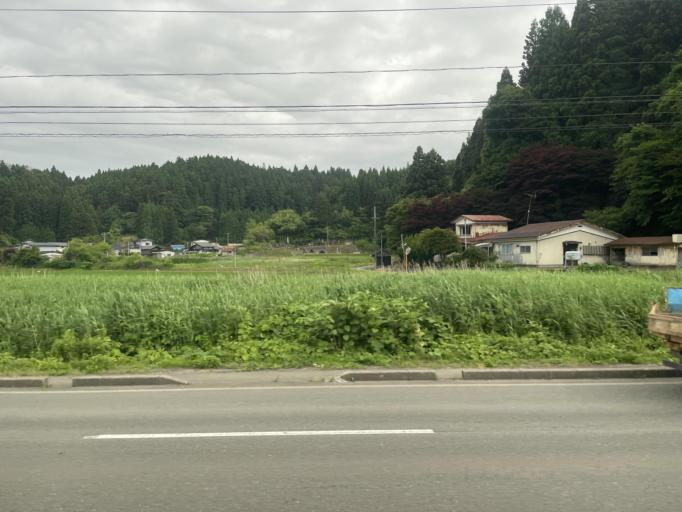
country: JP
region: Akita
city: Tenno
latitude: 39.9144
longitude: 139.8864
